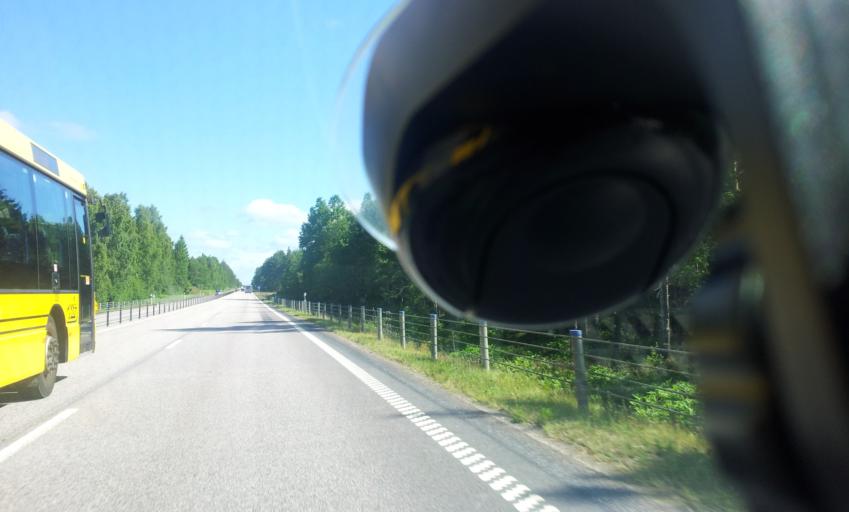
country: SE
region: Kalmar
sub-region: Monsteras Kommun
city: Timmernabben
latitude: 56.9913
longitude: 16.4110
